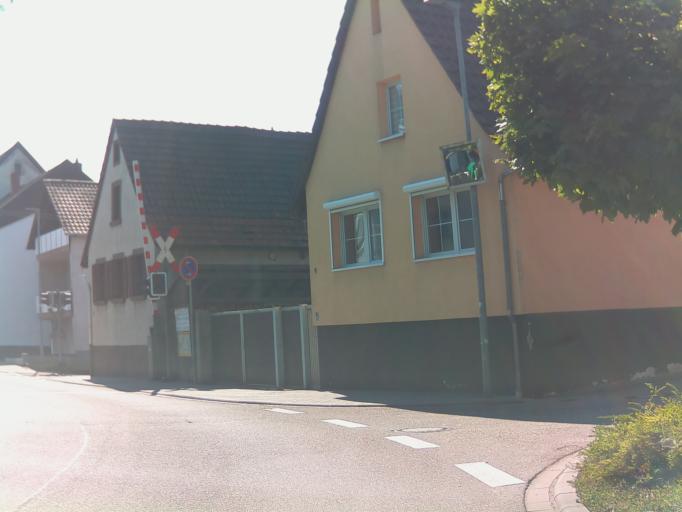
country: DE
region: Baden-Wuerttemberg
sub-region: Karlsruhe Region
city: Ubstadt-Weiher
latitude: 49.1787
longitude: 8.6771
